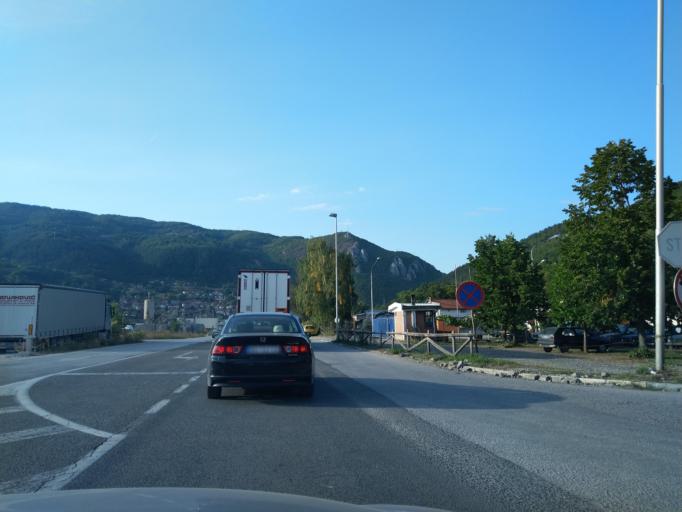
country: RS
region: Central Serbia
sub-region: Zlatiborski Okrug
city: Prijepolje
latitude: 43.3660
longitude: 19.6347
